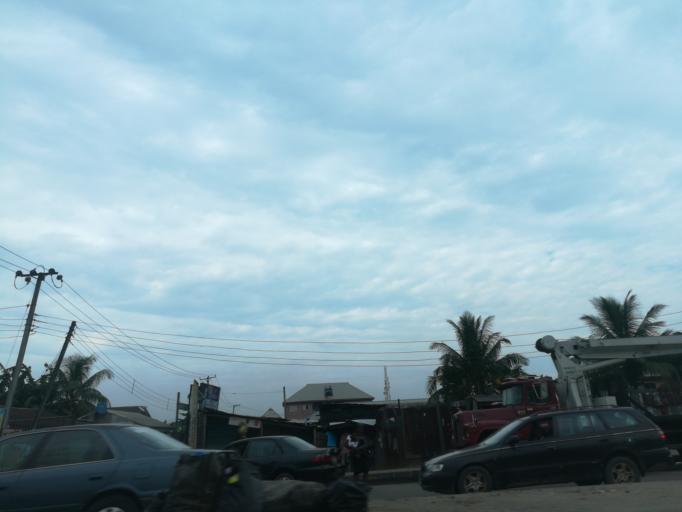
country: NG
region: Rivers
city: Port Harcourt
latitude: 4.8384
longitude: 6.9760
